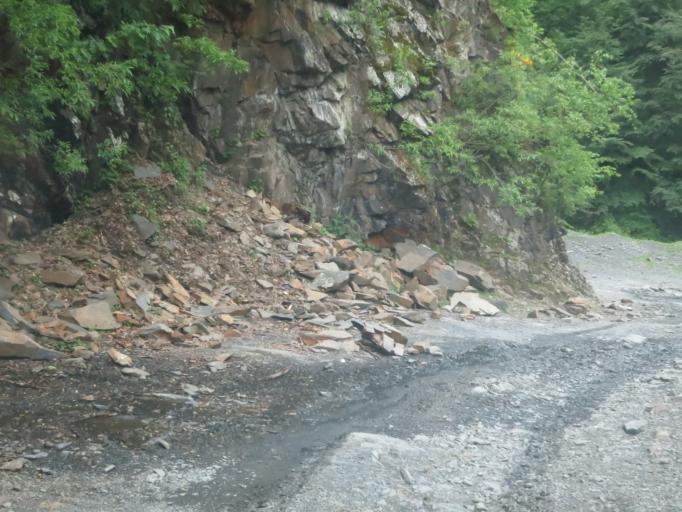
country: GE
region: Kakheti
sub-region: Telavi
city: Telavi
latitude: 42.2411
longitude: 45.4952
